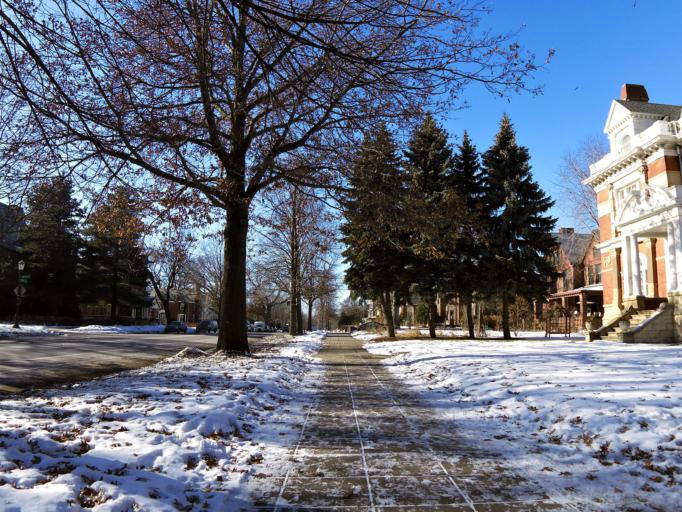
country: US
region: Minnesota
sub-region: Ramsey County
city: Saint Paul
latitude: 44.9415
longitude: -93.1195
